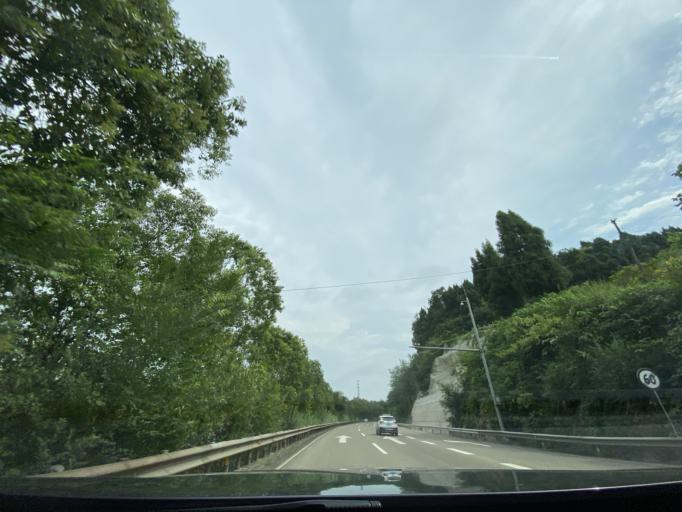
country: CN
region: Sichuan
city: Chonglong
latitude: 29.6855
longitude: 104.9520
